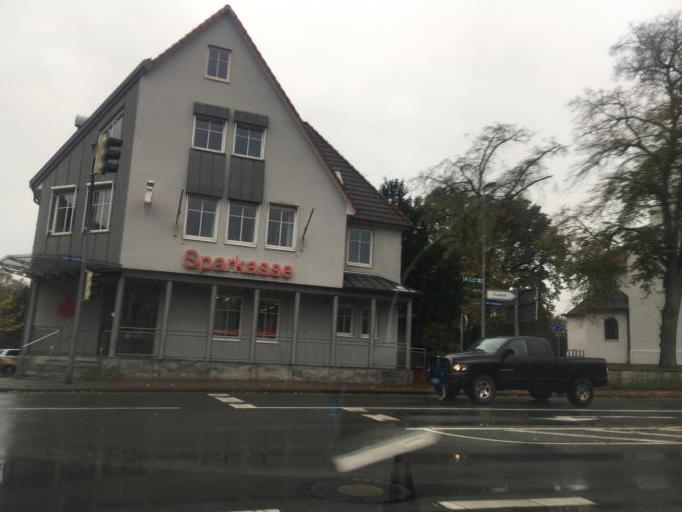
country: DE
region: Lower Saxony
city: Bergen
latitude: 52.8089
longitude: 9.9635
